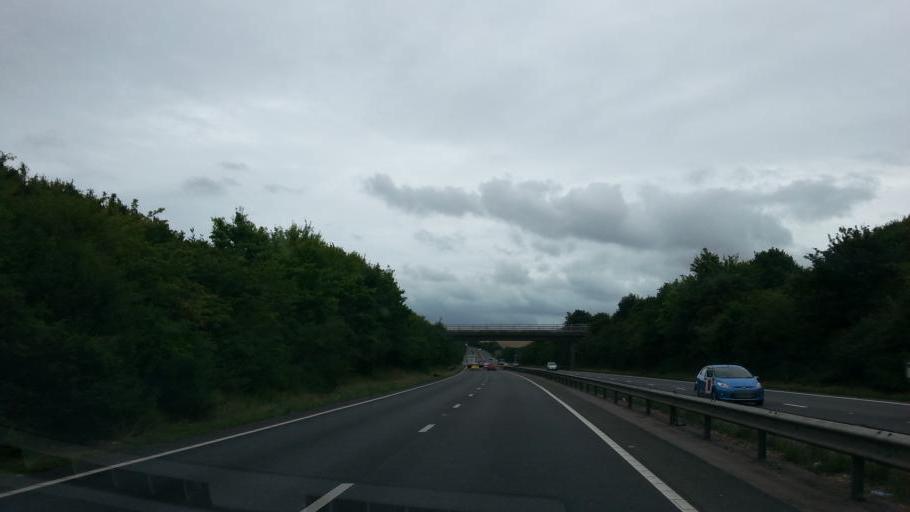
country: GB
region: England
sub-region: Oxfordshire
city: Harwell
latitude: 51.5591
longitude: -1.3010
